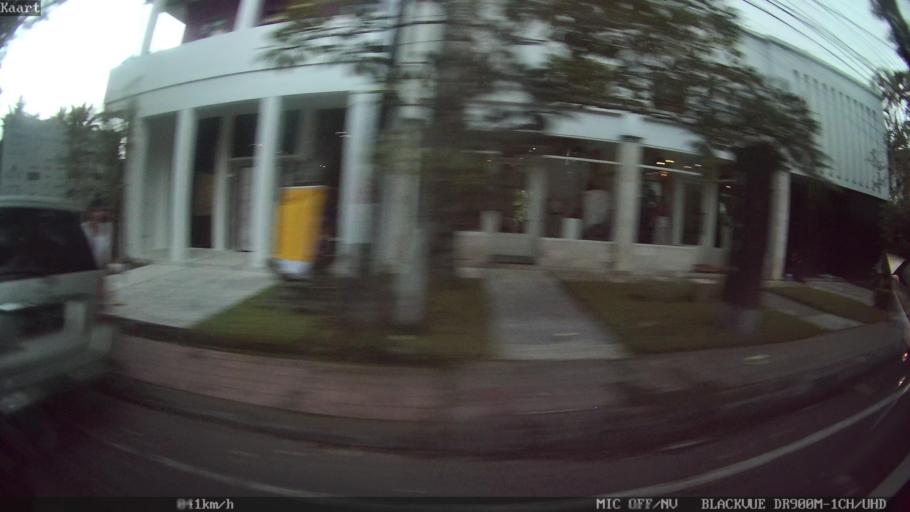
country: ID
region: Bali
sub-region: Kabupaten Gianyar
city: Ubud
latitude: -8.4928
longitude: 115.2534
